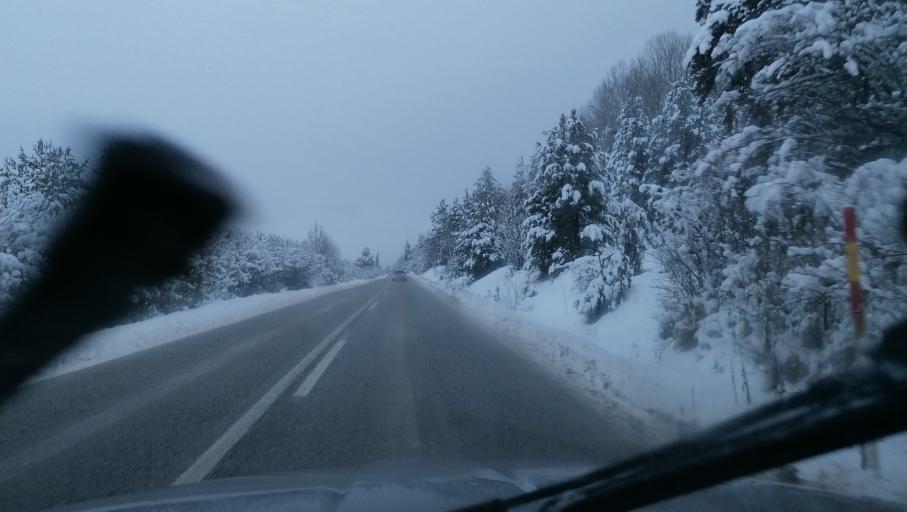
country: BA
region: Republika Srpska
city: Han Pijesak
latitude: 44.0117
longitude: 18.8876
